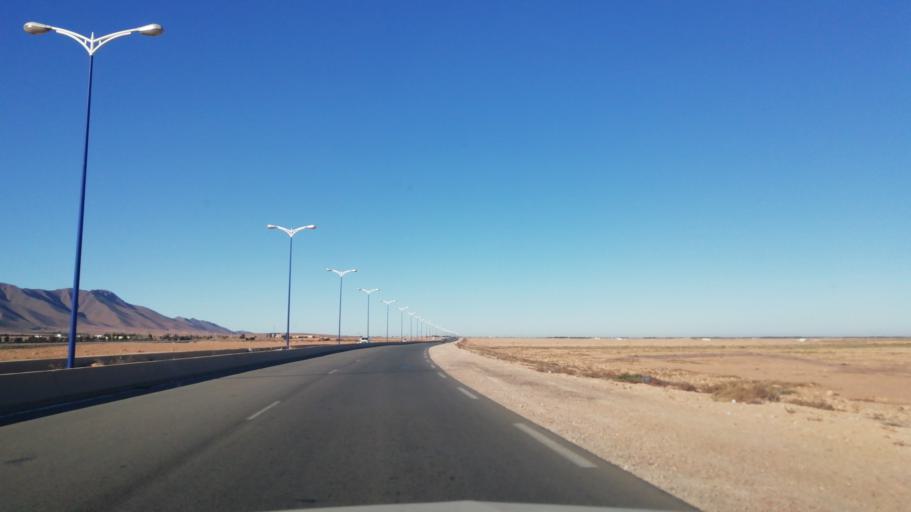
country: DZ
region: Wilaya de Naama
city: Naama
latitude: 33.5689
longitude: -0.2406
